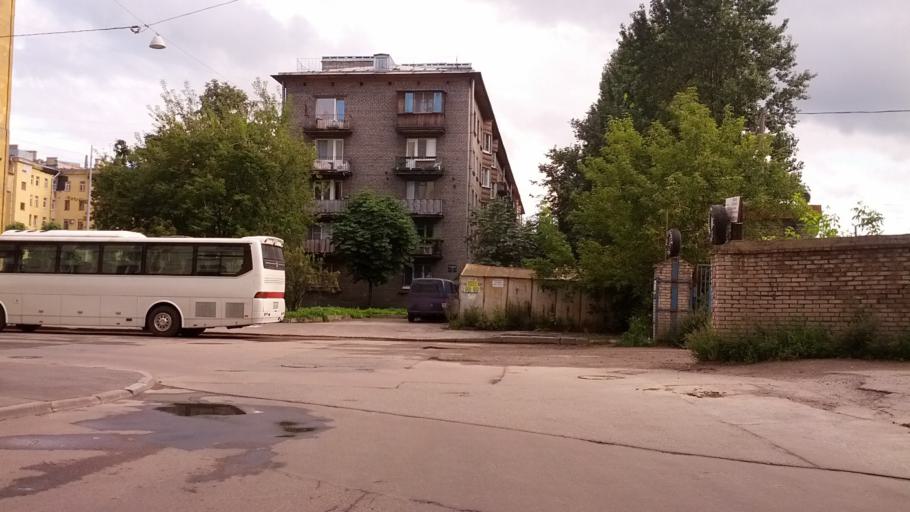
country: RU
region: St.-Petersburg
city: Admiralteisky
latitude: 59.9029
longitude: 30.3159
